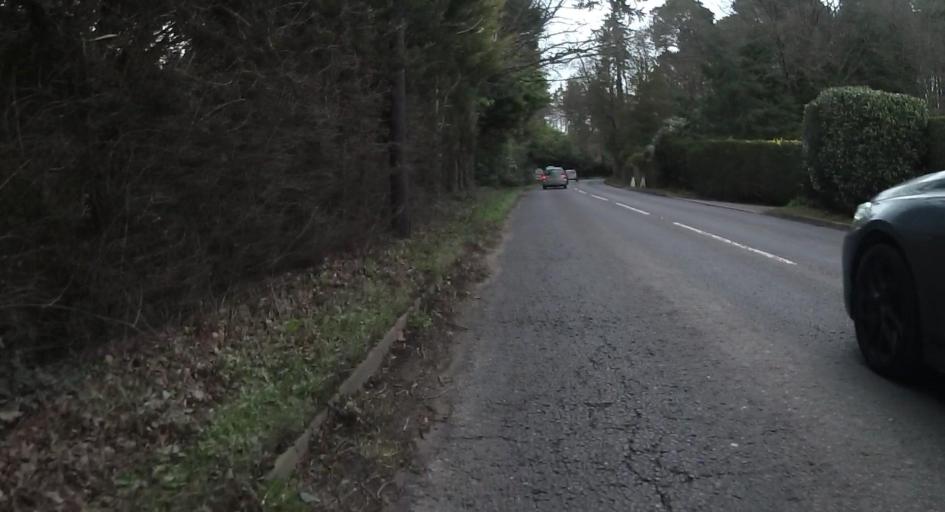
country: GB
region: England
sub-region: Surrey
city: Farnham
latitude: 51.1824
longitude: -0.7914
